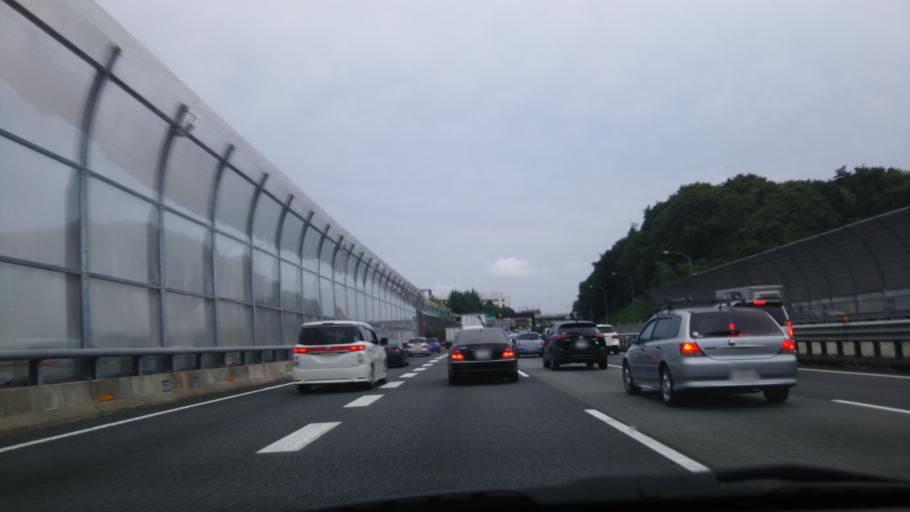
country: JP
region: Kanagawa
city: Atsugi
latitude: 35.4429
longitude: 139.4099
